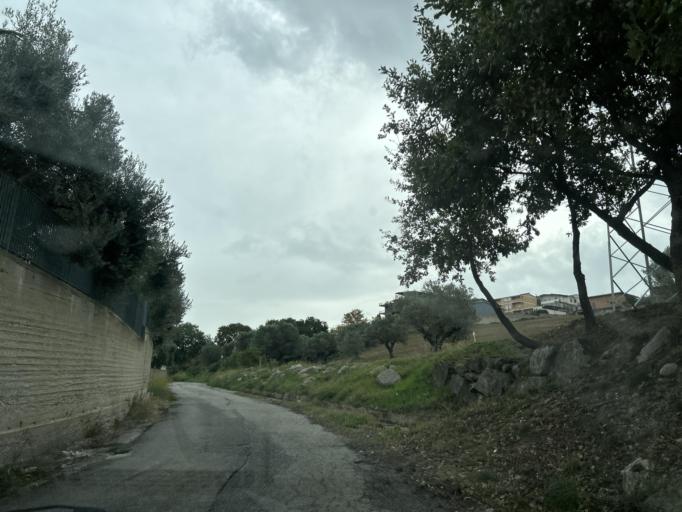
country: IT
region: Calabria
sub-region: Provincia di Catanzaro
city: Staletti
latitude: 38.7677
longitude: 16.5322
